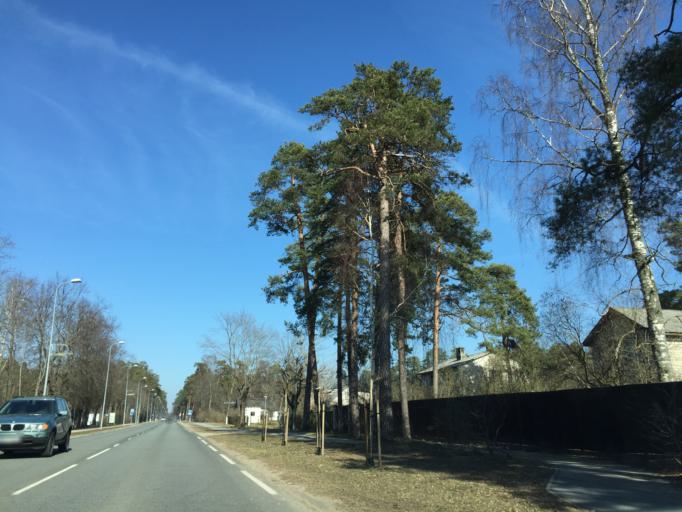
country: LV
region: Saulkrastu
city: Saulkrasti
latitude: 57.2454
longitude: 24.4041
